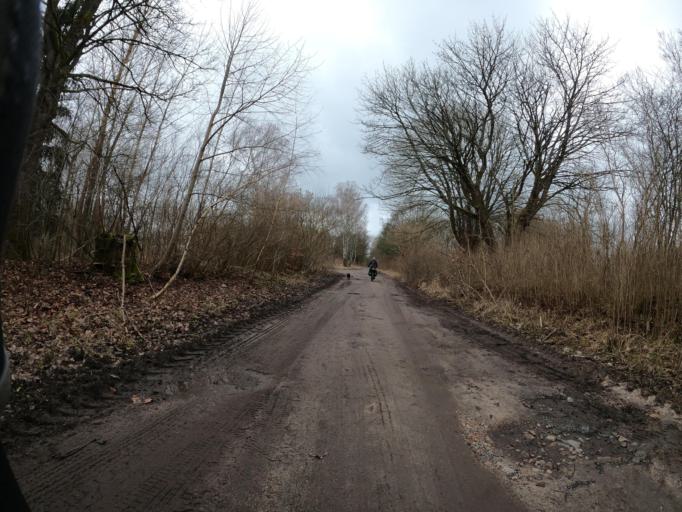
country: PL
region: Greater Poland Voivodeship
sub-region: Powiat zlotowski
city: Sypniewo
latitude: 53.4860
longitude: 16.5518
